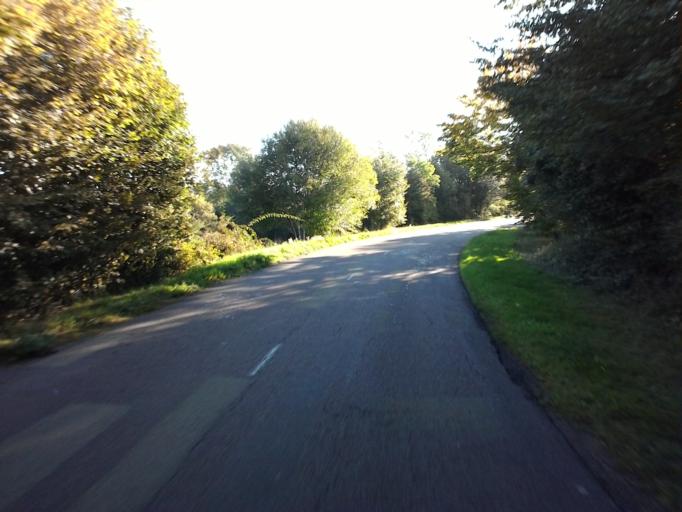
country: FR
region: Bourgogne
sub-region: Departement de la Cote-d'Or
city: Saulieu
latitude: 47.2756
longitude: 4.2210
